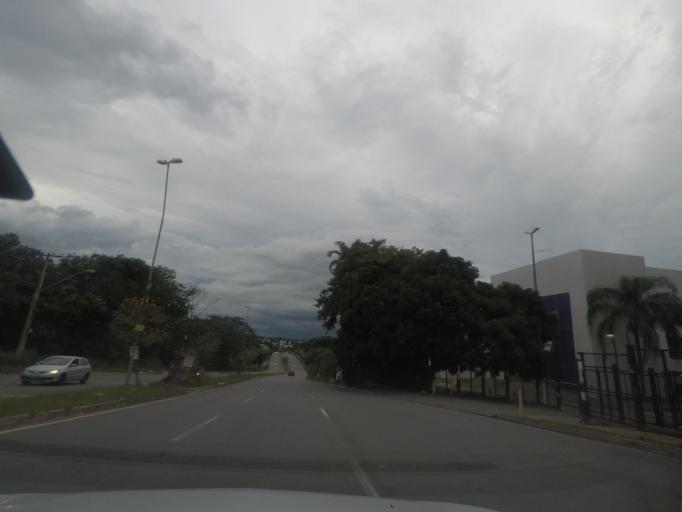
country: BR
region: Goias
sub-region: Goiania
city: Goiania
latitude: -16.7187
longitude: -49.2367
